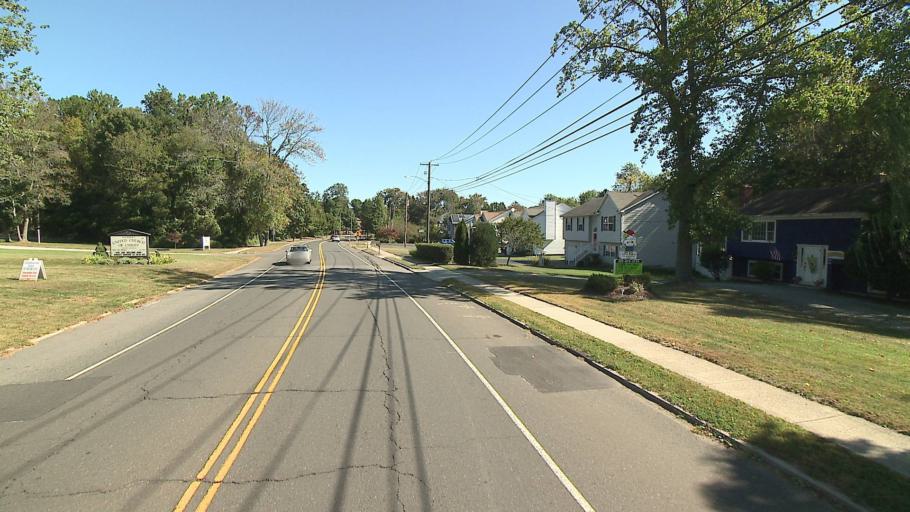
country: US
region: Connecticut
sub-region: New Haven County
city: Woodmont
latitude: 41.2270
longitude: -73.0130
